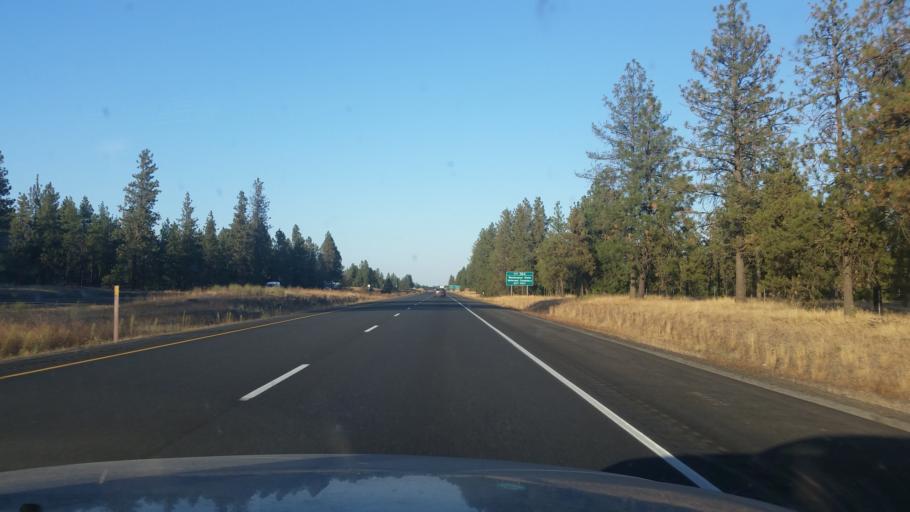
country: US
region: Washington
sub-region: Spokane County
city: Medical Lake
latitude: 47.4957
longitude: -117.7030
